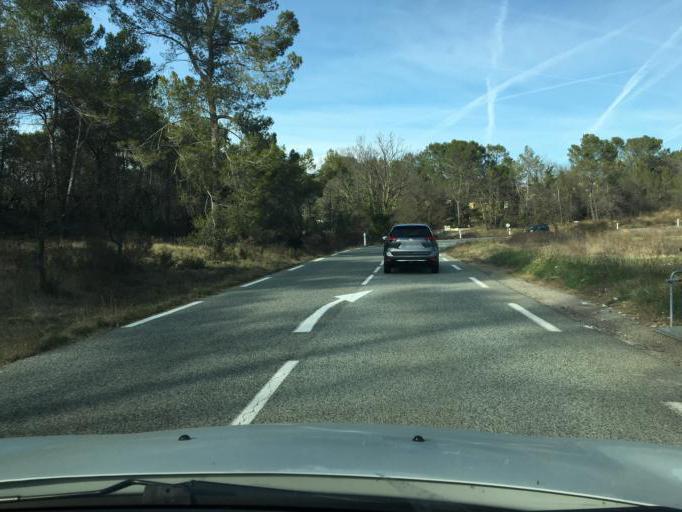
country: FR
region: Provence-Alpes-Cote d'Azur
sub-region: Departement du Var
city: Saint-Paul-en-Foret
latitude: 43.5893
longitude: 6.6763
